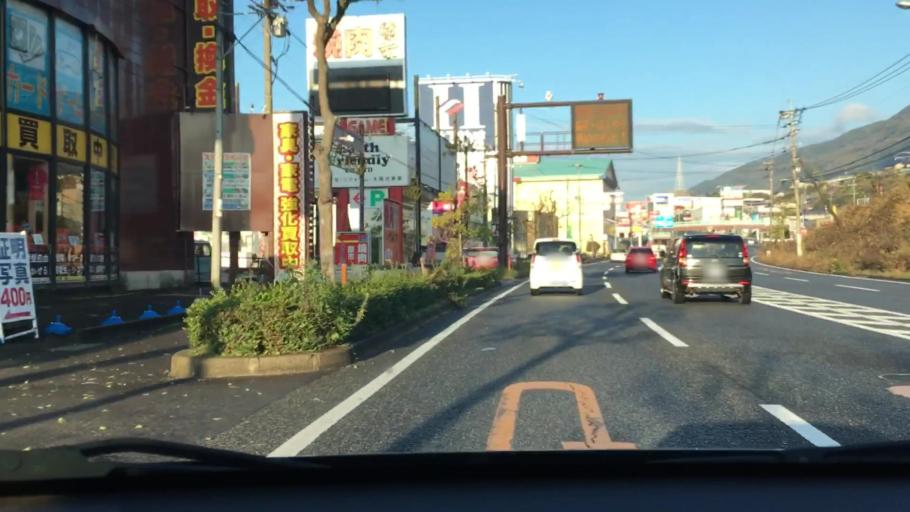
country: JP
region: Nagasaki
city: Sasebo
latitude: 33.1534
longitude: 129.7743
